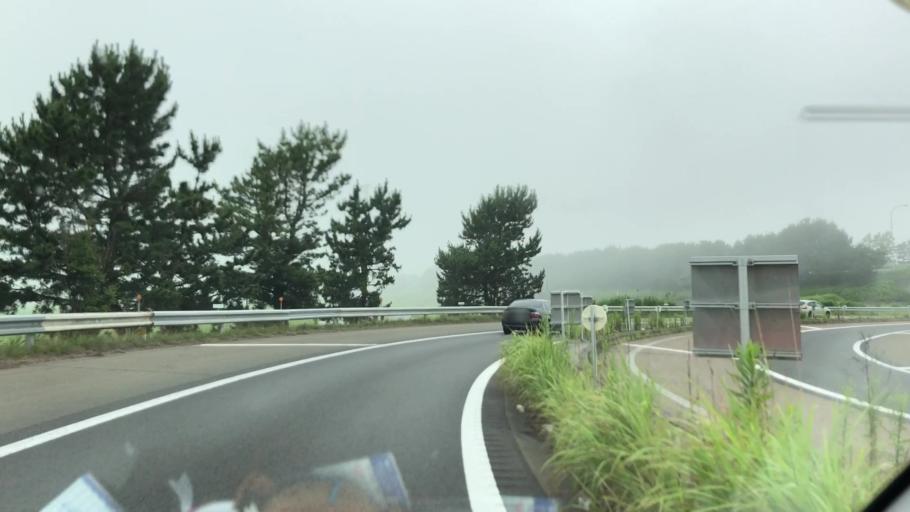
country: JP
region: Miyagi
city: Sendai
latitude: 38.2077
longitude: 140.9466
